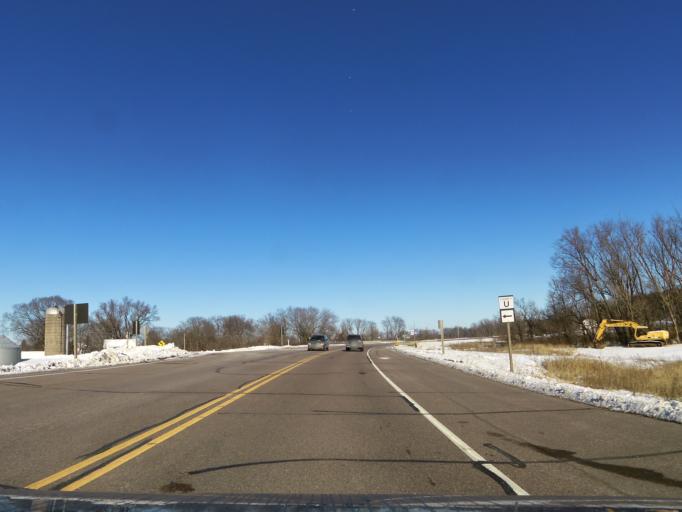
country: US
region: Wisconsin
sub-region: Sauk County
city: Baraboo
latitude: 43.5026
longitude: -89.6338
